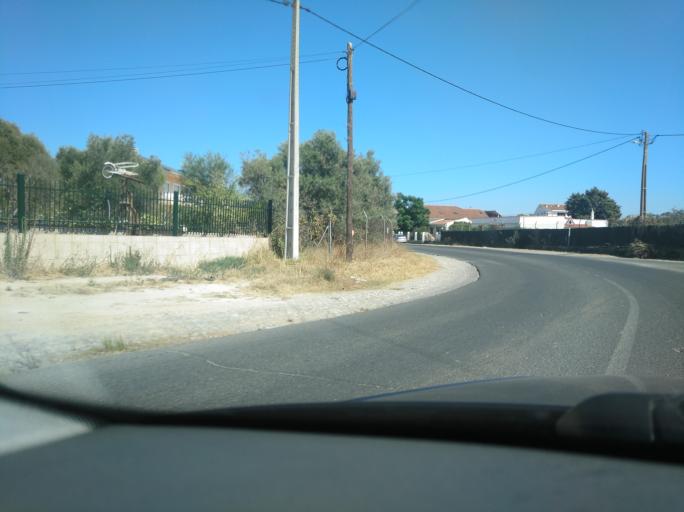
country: PT
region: Faro
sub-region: Olhao
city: Olhao
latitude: 37.0442
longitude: -7.8610
